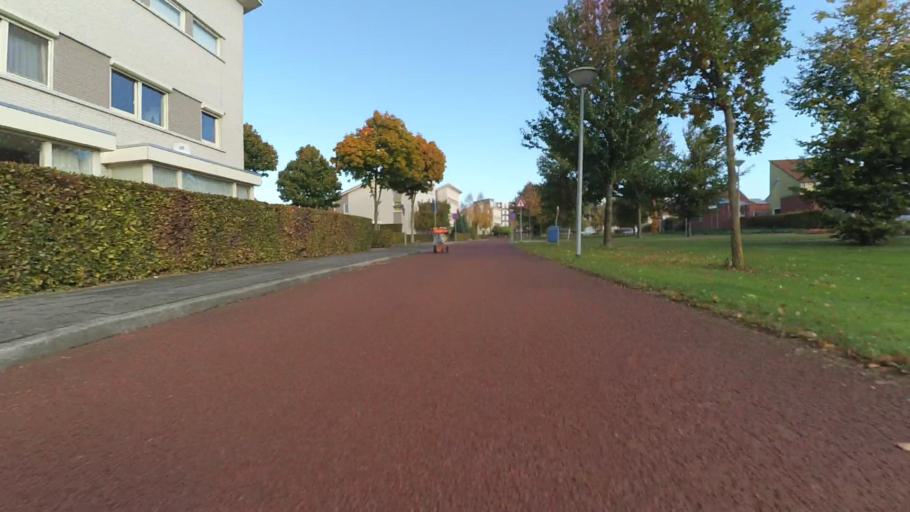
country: NL
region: Gelderland
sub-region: Gemeente Ermelo
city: Horst
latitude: 52.3241
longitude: 5.5944
